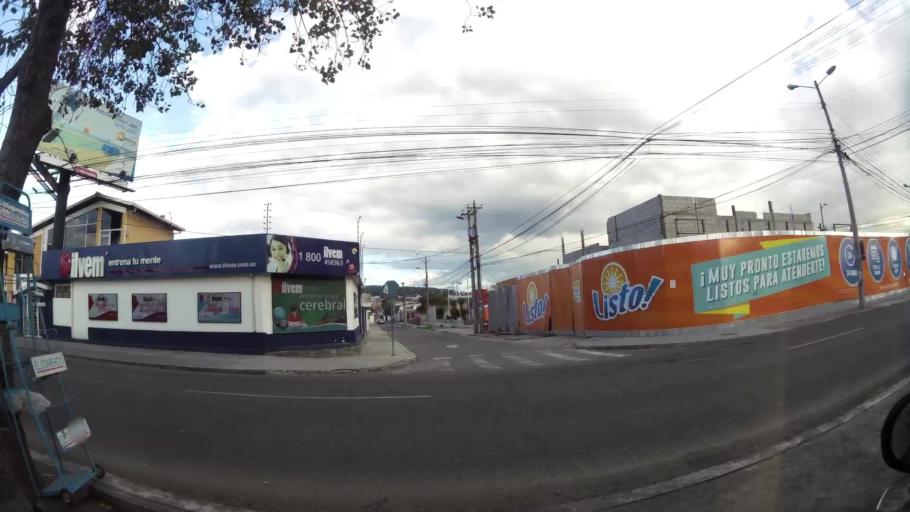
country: EC
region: Pichincha
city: Quito
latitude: -0.1587
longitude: -78.4833
